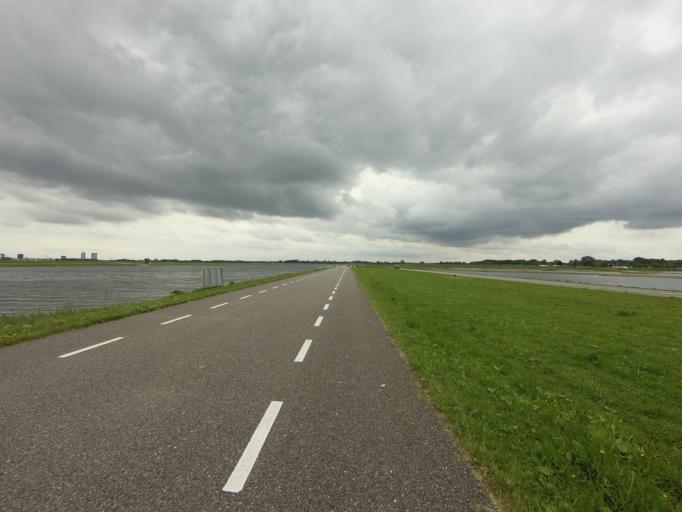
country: NL
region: South Holland
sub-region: Gemeente Lansingerland
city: Bleiswijk
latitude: 52.0039
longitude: 4.5623
